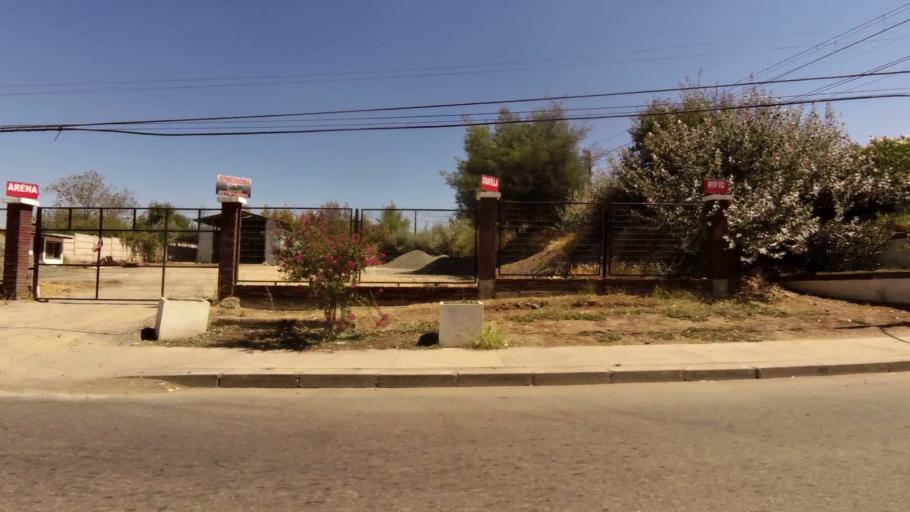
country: CL
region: Maule
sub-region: Provincia de Talca
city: Talca
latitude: -35.3035
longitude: -71.5162
